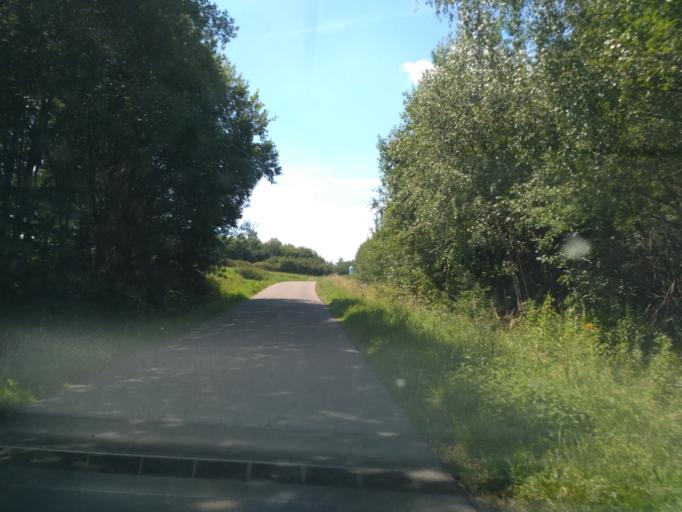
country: PL
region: Subcarpathian Voivodeship
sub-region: Powiat strzyzowski
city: Jawornik
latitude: 49.8592
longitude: 21.8803
